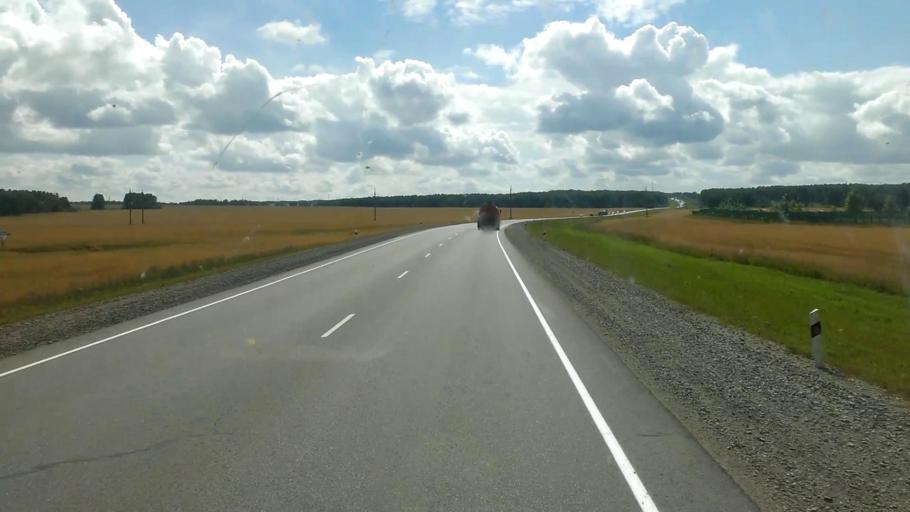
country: RU
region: Altai Krai
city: Troitskoye
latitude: 52.9938
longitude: 84.7406
